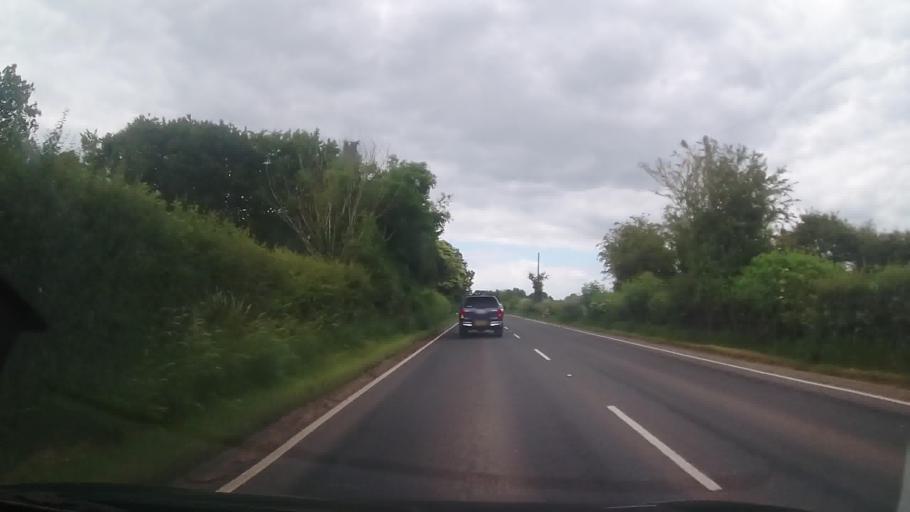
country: GB
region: England
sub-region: Herefordshire
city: Hereford
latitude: 52.0842
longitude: -2.7229
